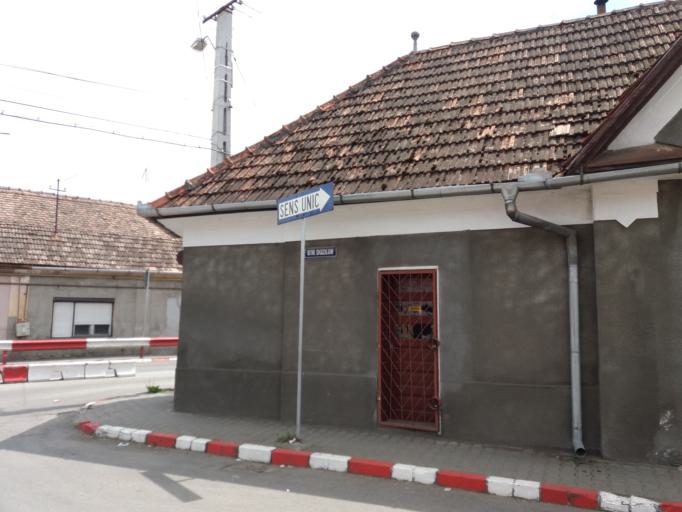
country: RO
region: Mures
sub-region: Municipiul Reghin
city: Reghin
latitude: 46.7778
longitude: 24.7087
